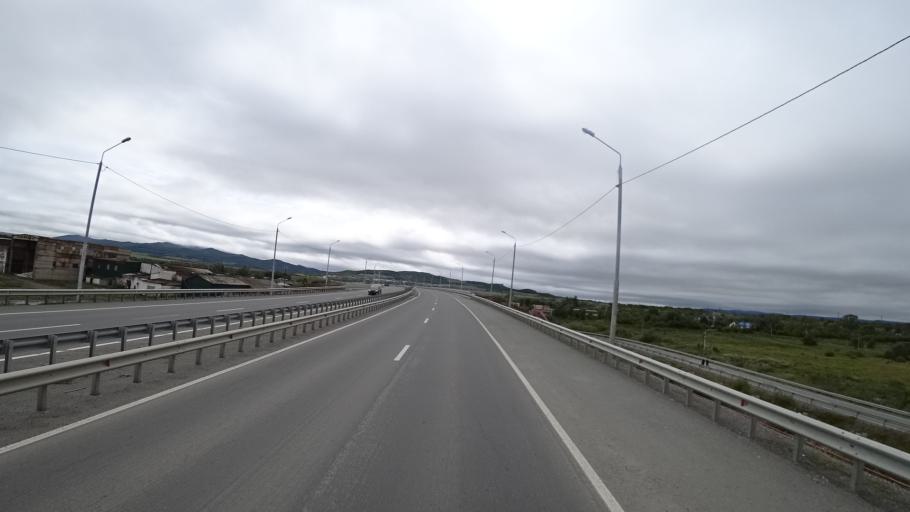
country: RU
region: Primorskiy
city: Monastyrishche
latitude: 44.1938
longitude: 132.4429
